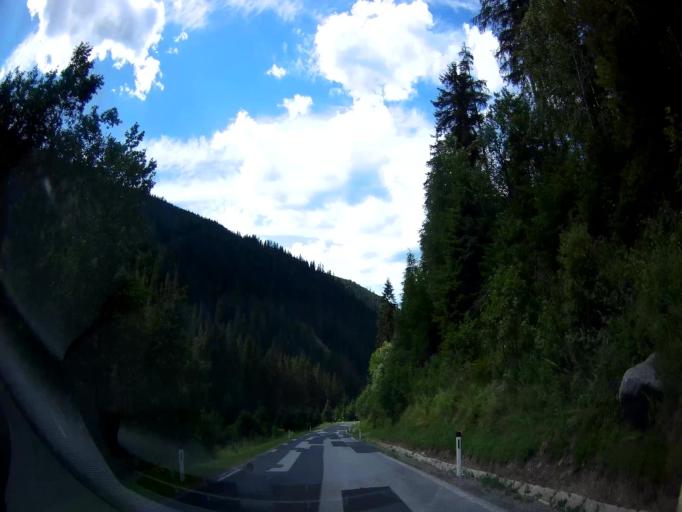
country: AT
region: Styria
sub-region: Politischer Bezirk Murau
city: Stadl an der Mur
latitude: 47.0305
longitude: 14.0082
